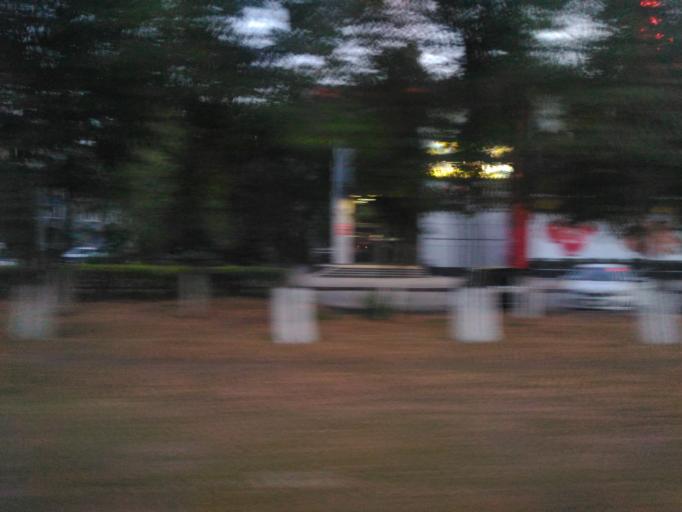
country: RU
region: Ulyanovsk
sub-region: Ulyanovskiy Rayon
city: Ulyanovsk
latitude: 54.3079
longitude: 48.3356
